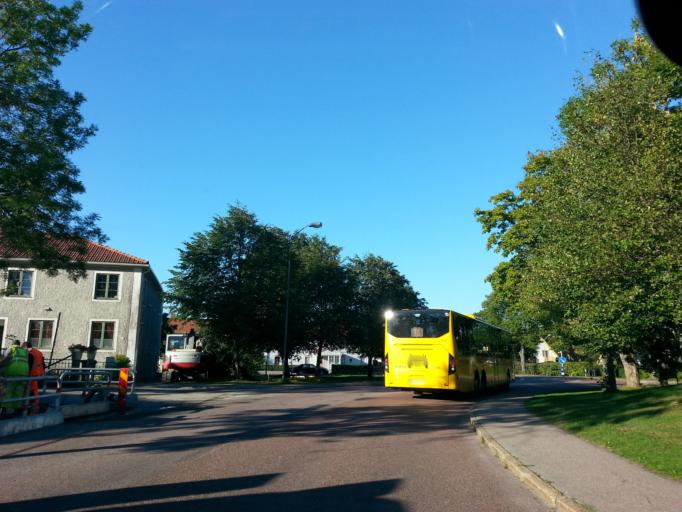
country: SE
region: Uppsala
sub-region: Osthammars Kommun
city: Oregrund
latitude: 60.3377
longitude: 18.4385
